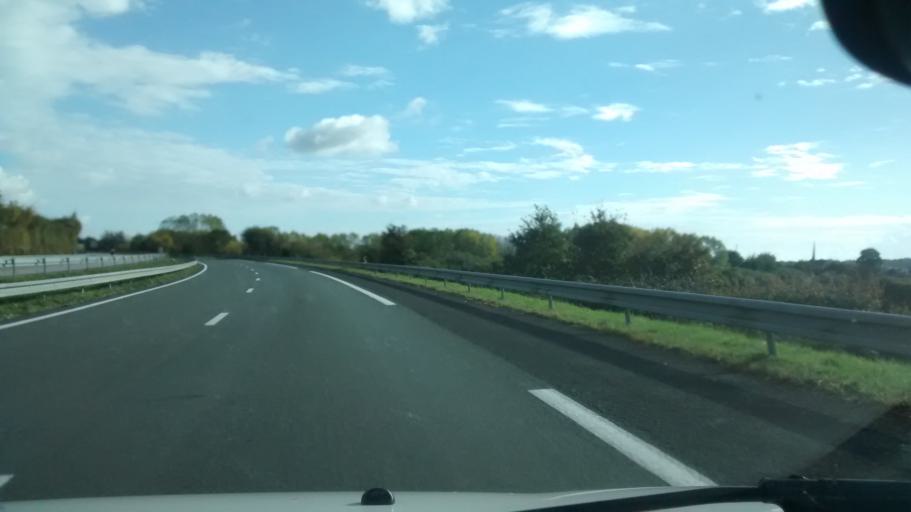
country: FR
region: Pays de la Loire
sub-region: Departement de Maine-et-Loire
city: Pouance
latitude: 47.7580
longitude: -1.1873
